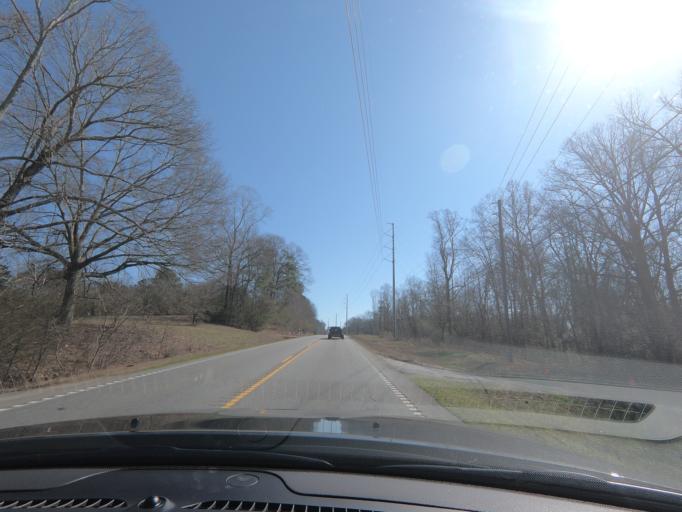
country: US
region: Georgia
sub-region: Forsyth County
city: Cumming
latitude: 34.3009
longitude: -84.1843
